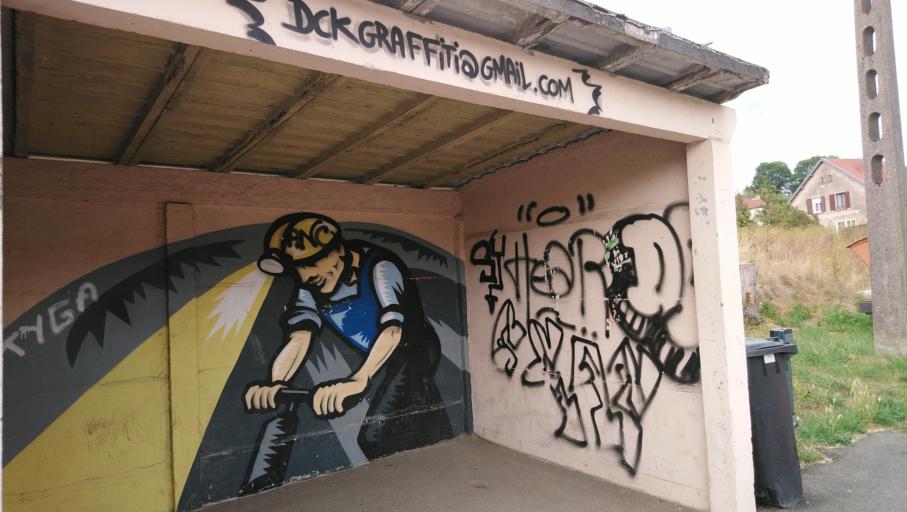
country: LU
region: Luxembourg
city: Belvaux
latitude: 49.4988
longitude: 5.9179
